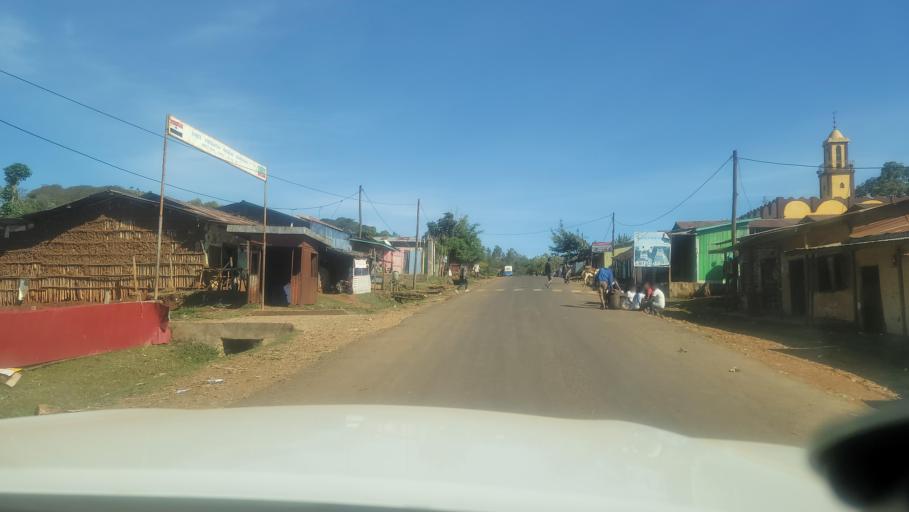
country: ET
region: Oromiya
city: Agaro
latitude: 7.7966
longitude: 36.4774
